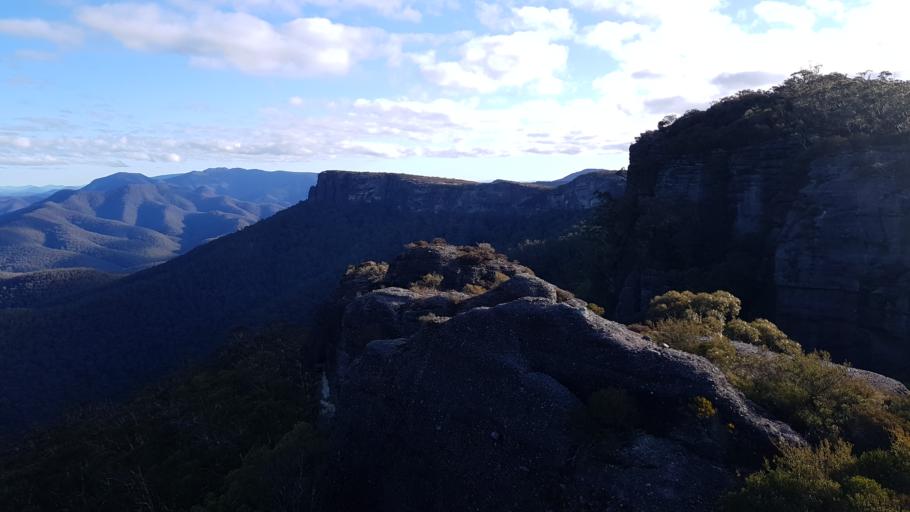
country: AU
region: New South Wales
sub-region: Shoalhaven Shire
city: Milton
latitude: -35.2795
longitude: 150.1337
